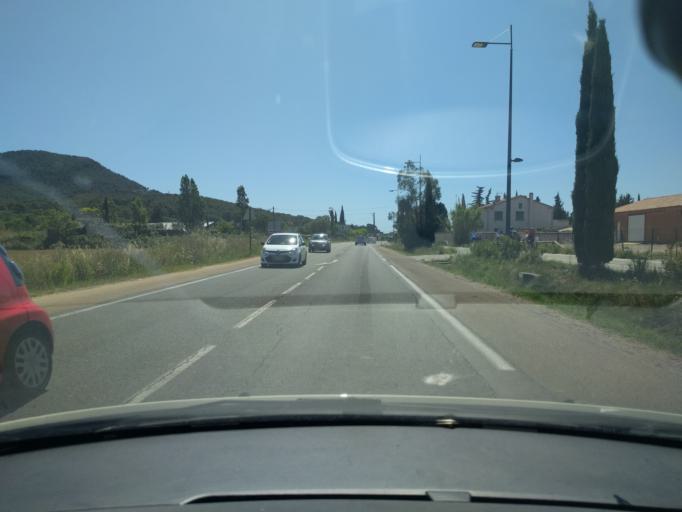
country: FR
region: Provence-Alpes-Cote d'Azur
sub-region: Departement du Var
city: Carqueiranne
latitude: 43.1073
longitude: 6.0502
